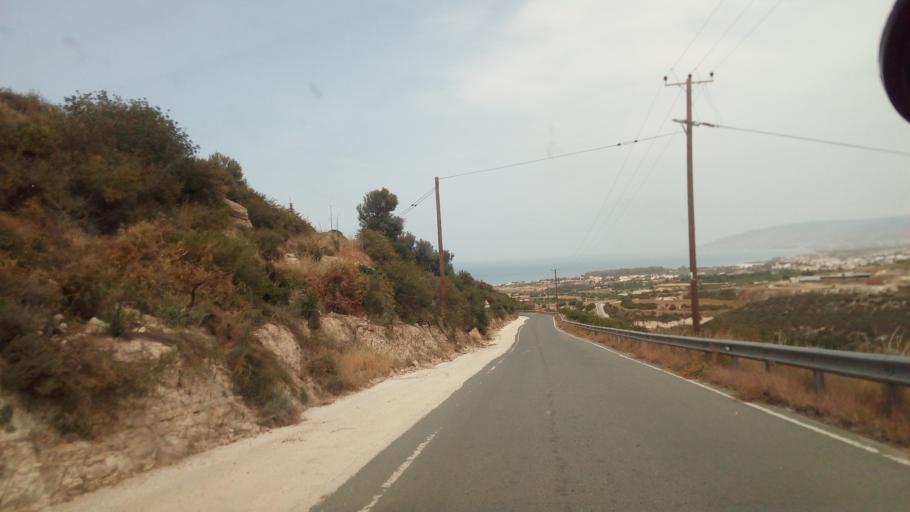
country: CY
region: Pafos
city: Polis
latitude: 35.0152
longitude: 32.3959
